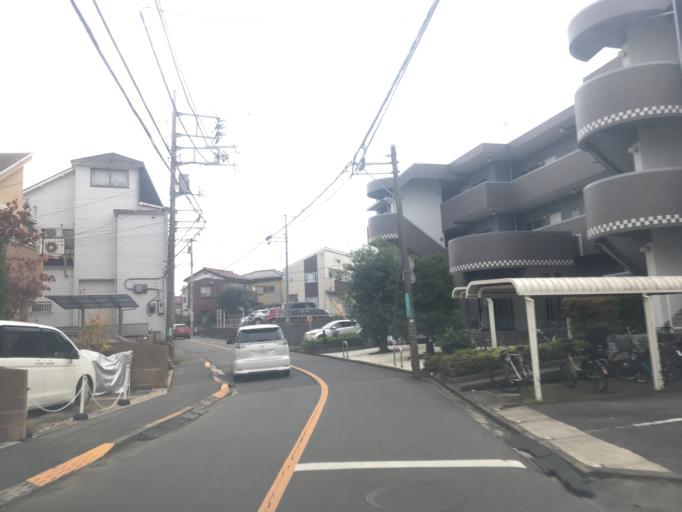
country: JP
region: Tokyo
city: Higashimurayama-shi
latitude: 35.7633
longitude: 139.4557
